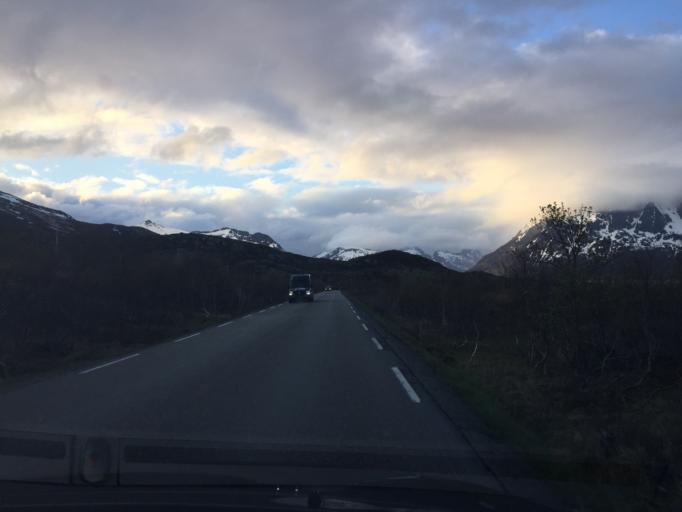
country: NO
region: Nordland
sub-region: Vagan
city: Svolvaer
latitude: 68.2909
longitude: 14.6971
